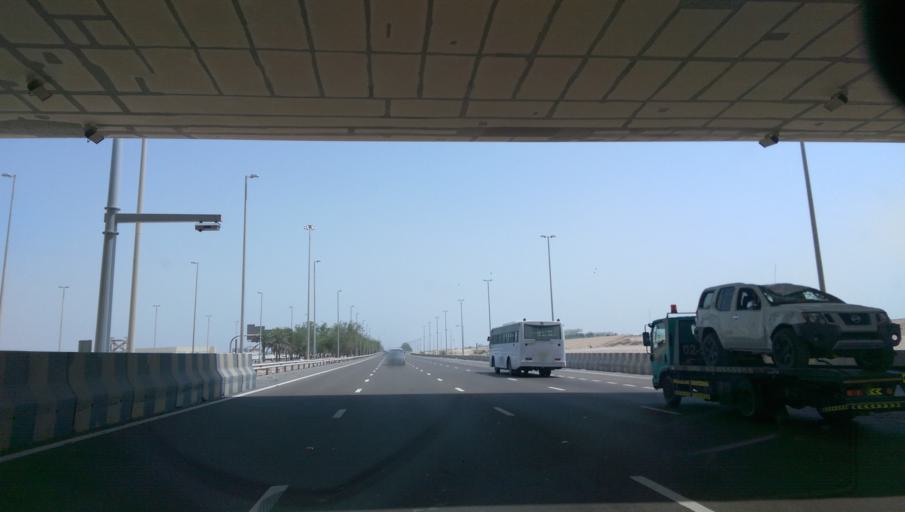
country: AE
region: Abu Dhabi
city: Abu Dhabi
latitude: 24.4306
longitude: 54.6781
